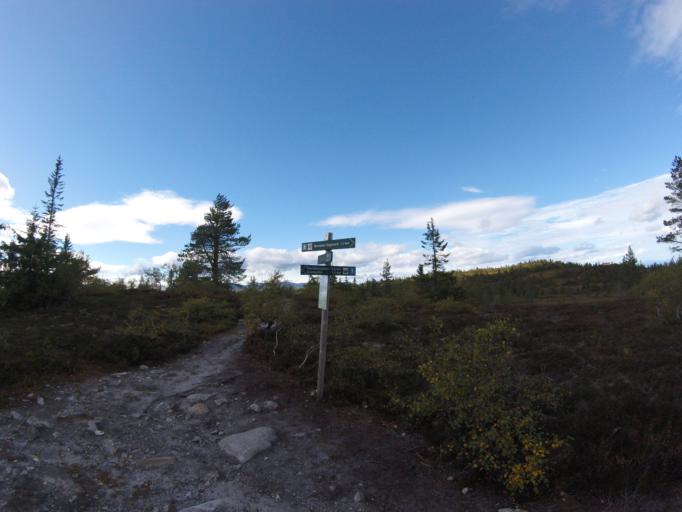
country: NO
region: Buskerud
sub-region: Flesberg
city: Lampeland
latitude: 59.7631
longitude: 9.4245
